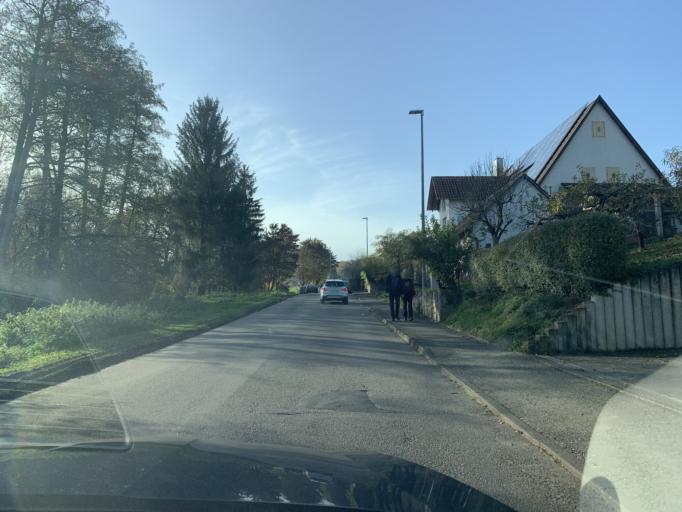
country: DE
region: Baden-Wuerttemberg
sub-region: Regierungsbezirk Stuttgart
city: Unterensingen
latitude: 48.6522
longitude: 9.3464
